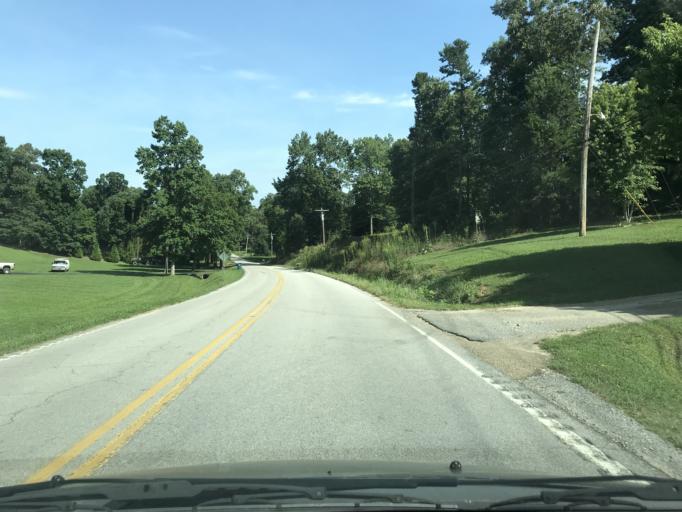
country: US
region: Tennessee
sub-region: Hamilton County
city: Lakesite
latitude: 35.2296
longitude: -85.0624
